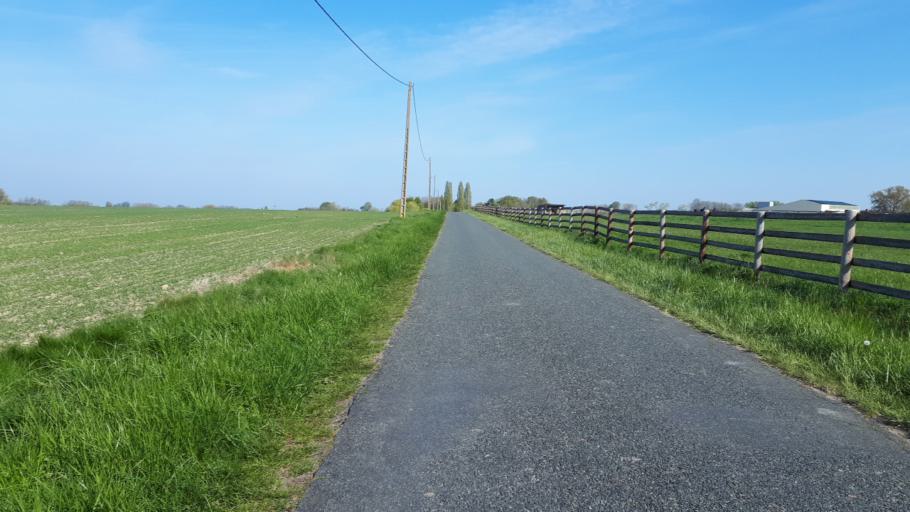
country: FR
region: Centre
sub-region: Departement du Loir-et-Cher
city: Contres
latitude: 47.3734
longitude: 1.3974
